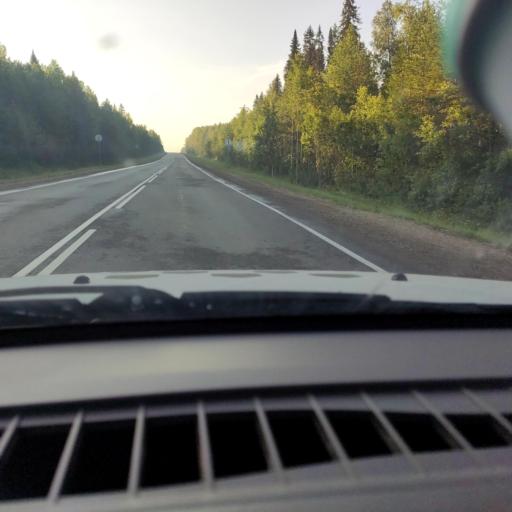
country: RU
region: Kirov
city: Chernaya Kholunitsa
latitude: 58.8202
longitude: 51.8111
